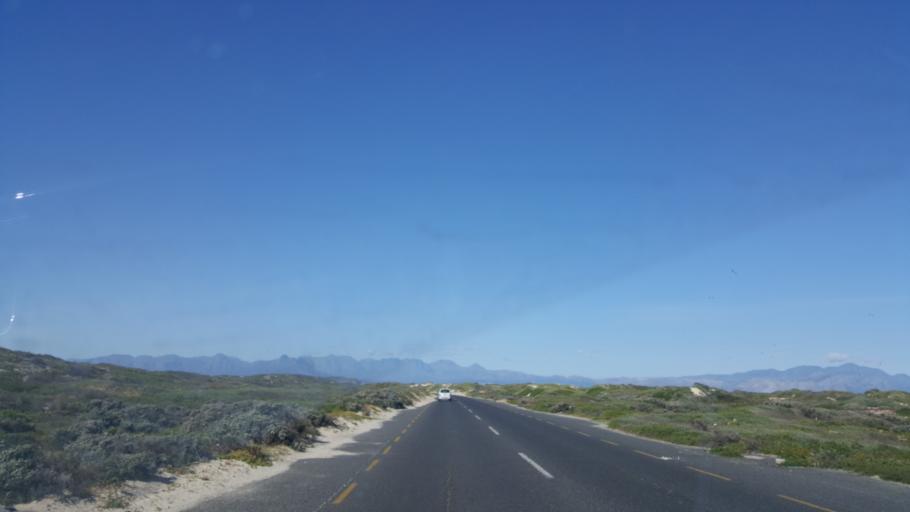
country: ZA
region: Western Cape
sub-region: City of Cape Town
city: Retreat
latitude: -34.0770
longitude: 18.5953
